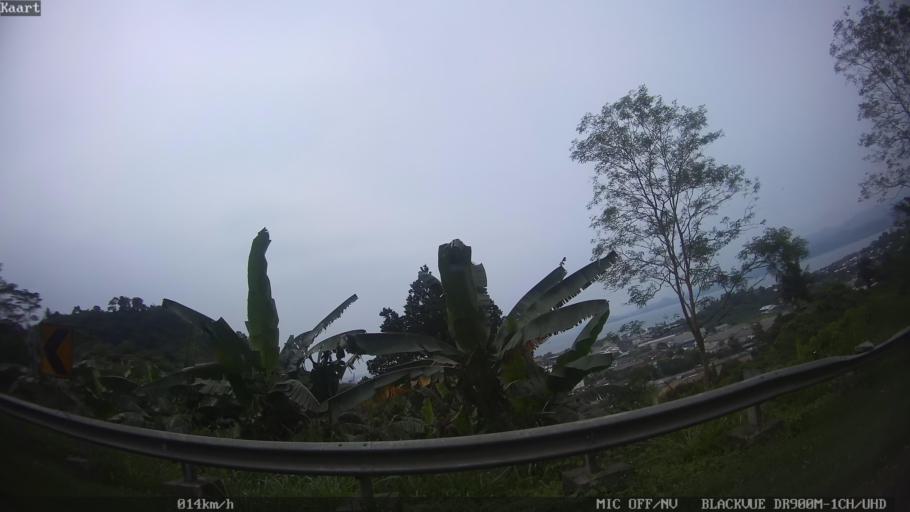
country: ID
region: Lampung
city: Panjang
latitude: -5.4417
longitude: 105.3141
